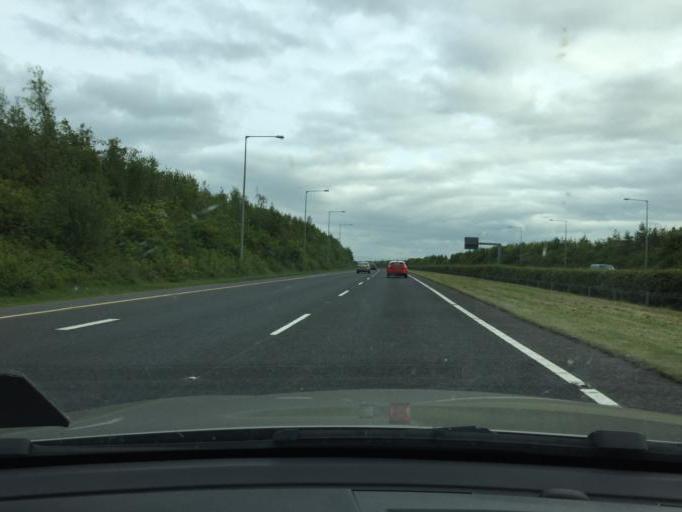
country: IE
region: Leinster
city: Balrothery
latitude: 53.5579
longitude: -6.2151
